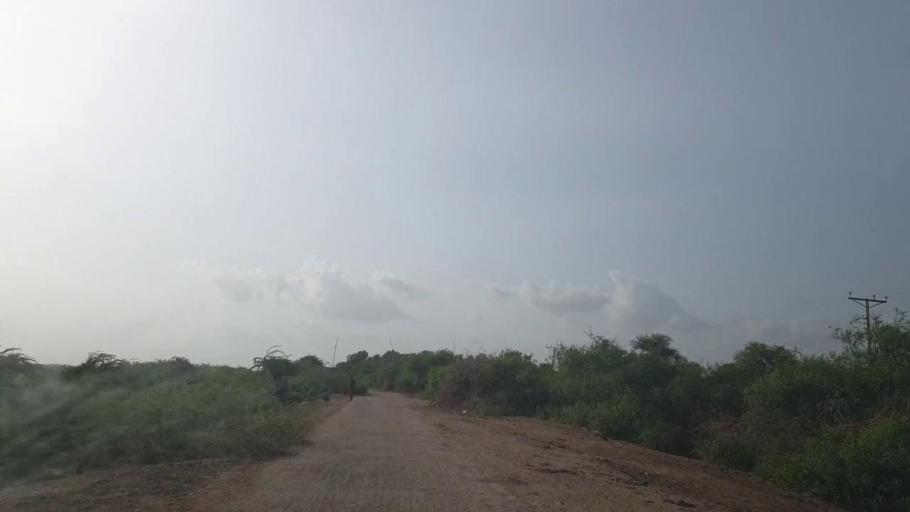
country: PK
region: Sindh
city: Tando Bago
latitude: 24.7559
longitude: 69.0849
